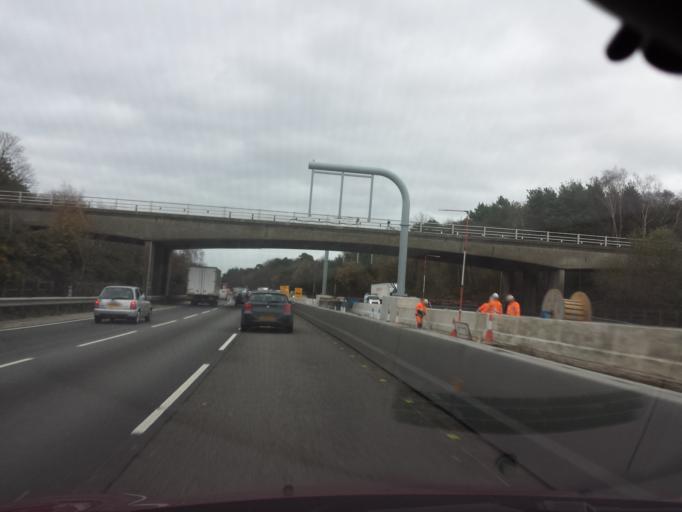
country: GB
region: England
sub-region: Surrey
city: Chobham
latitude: 51.3775
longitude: -0.5973
